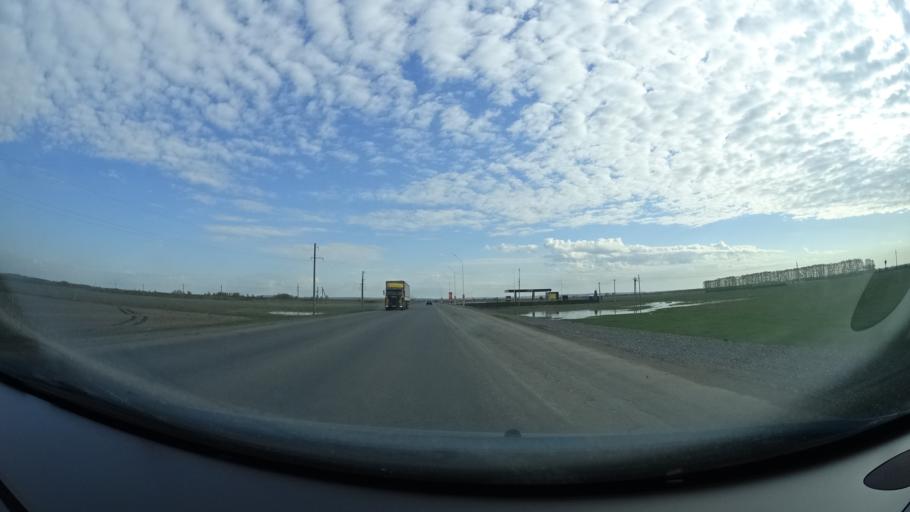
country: RU
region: Bashkortostan
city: Mikhaylovka
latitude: 54.9665
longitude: 55.7630
